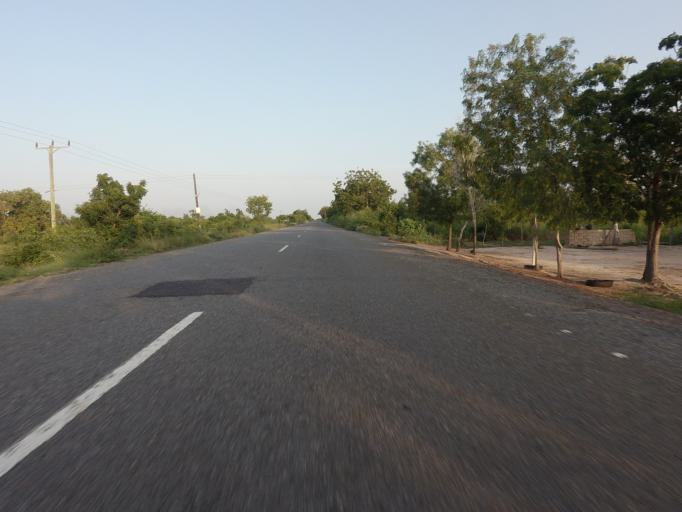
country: GH
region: Volta
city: Anloga
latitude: 5.8593
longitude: 0.7649
